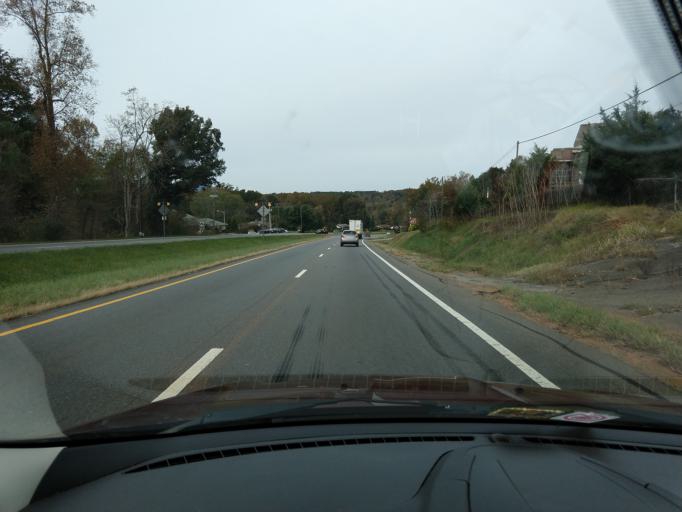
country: US
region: Virginia
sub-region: Franklin County
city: Rocky Mount
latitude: 37.0476
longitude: -79.8798
